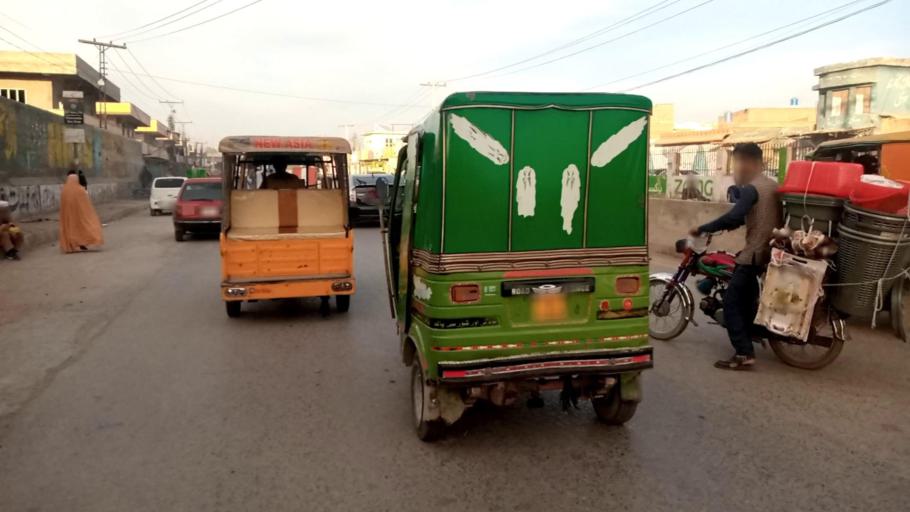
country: PK
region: Khyber Pakhtunkhwa
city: Peshawar
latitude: 34.0303
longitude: 71.5765
